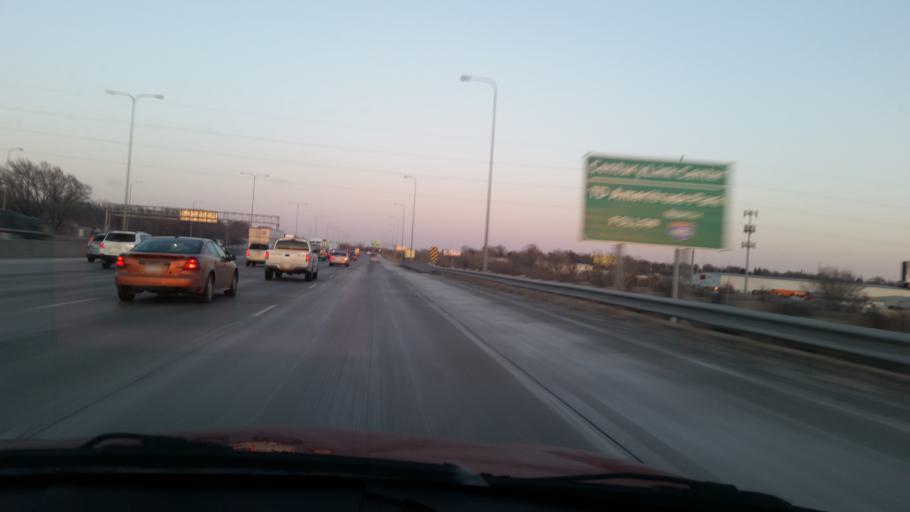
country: US
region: Nebraska
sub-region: Douglas County
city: Ralston
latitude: 41.2224
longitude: -95.9914
